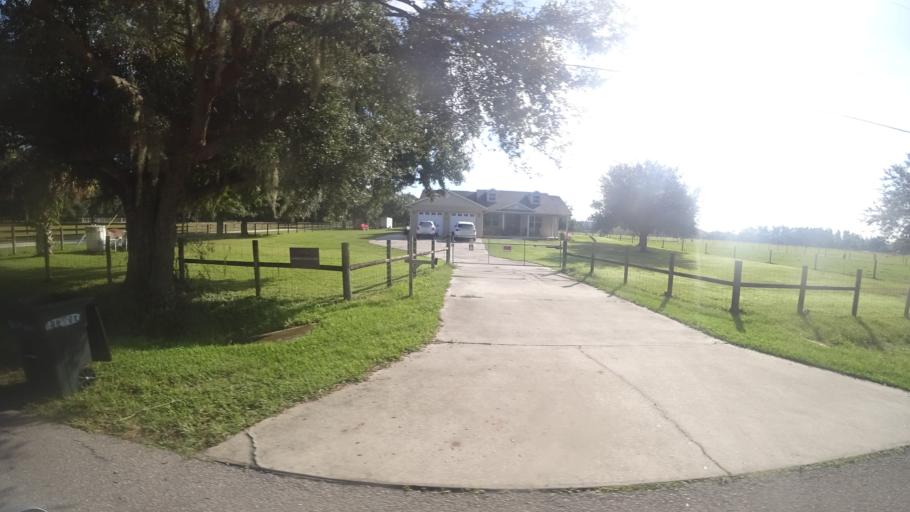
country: US
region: Florida
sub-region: Manatee County
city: Ellenton
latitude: 27.5607
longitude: -82.3924
